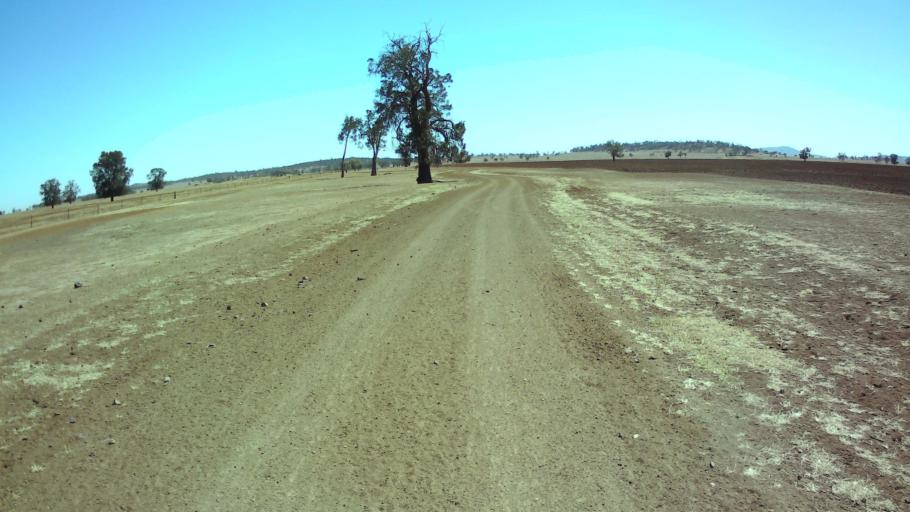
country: AU
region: New South Wales
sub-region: Forbes
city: Forbes
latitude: -33.7116
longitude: 147.6673
